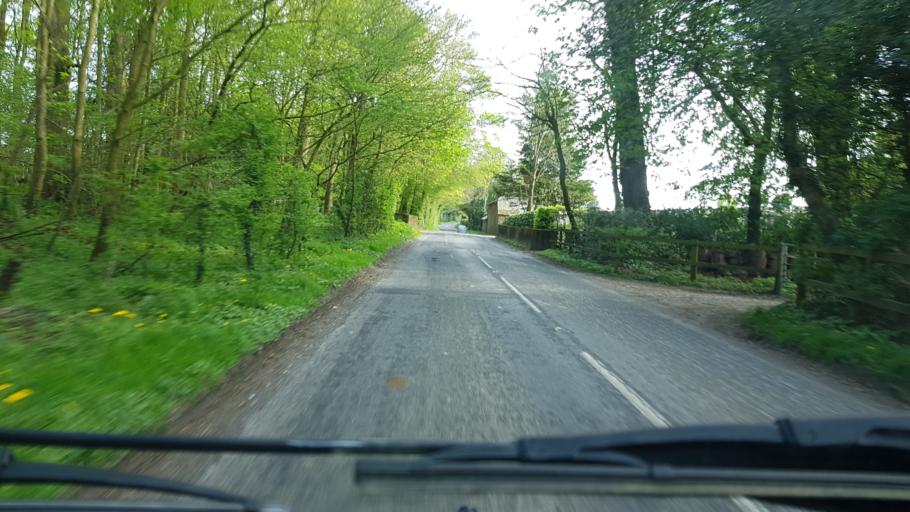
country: GB
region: England
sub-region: Hampshire
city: Kingsclere
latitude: 51.2890
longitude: -1.2639
